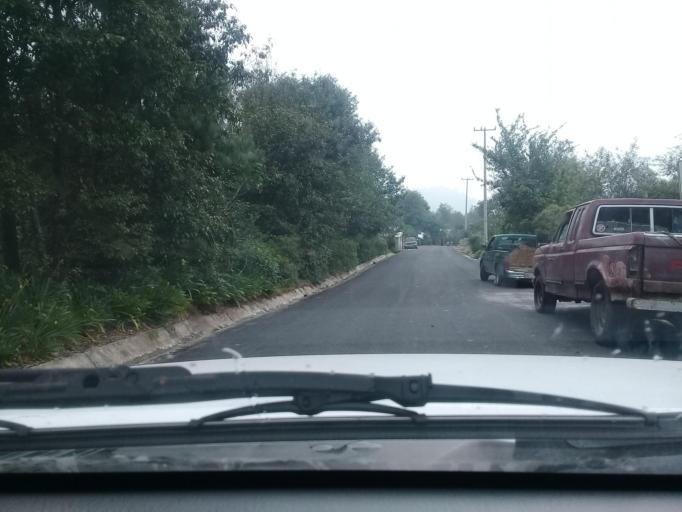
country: MX
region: Veracruz
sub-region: Mariano Escobedo
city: San Isidro el Berro
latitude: 18.9489
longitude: -97.2090
